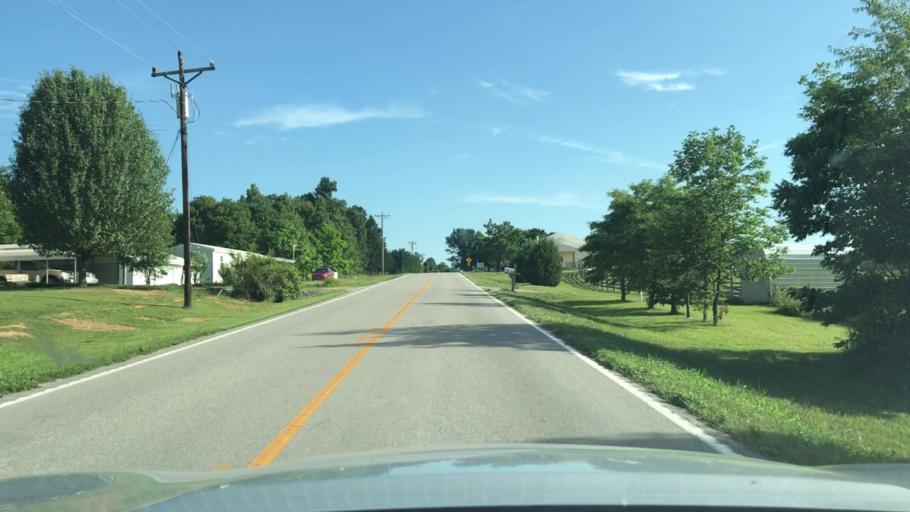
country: US
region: Kentucky
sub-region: Todd County
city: Elkton
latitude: 36.9270
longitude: -87.1623
